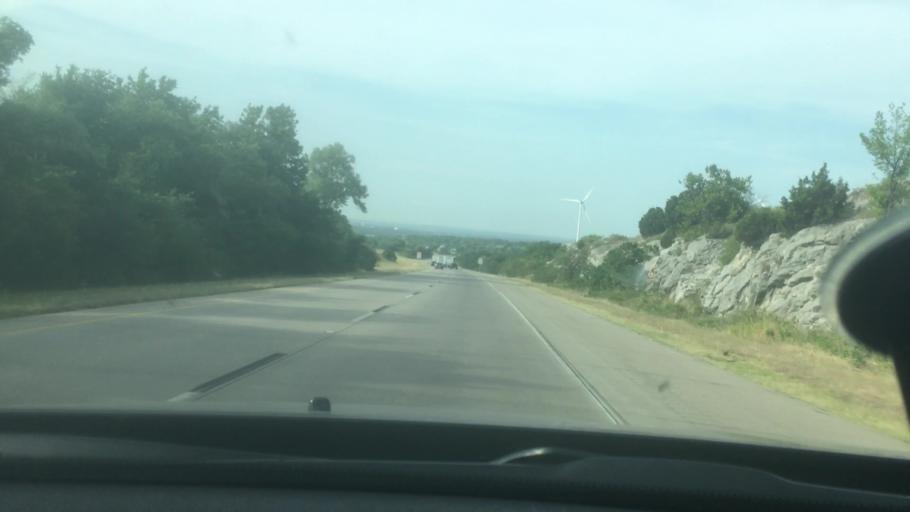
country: US
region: Oklahoma
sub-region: Murray County
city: Davis
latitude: 34.3727
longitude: -97.1459
